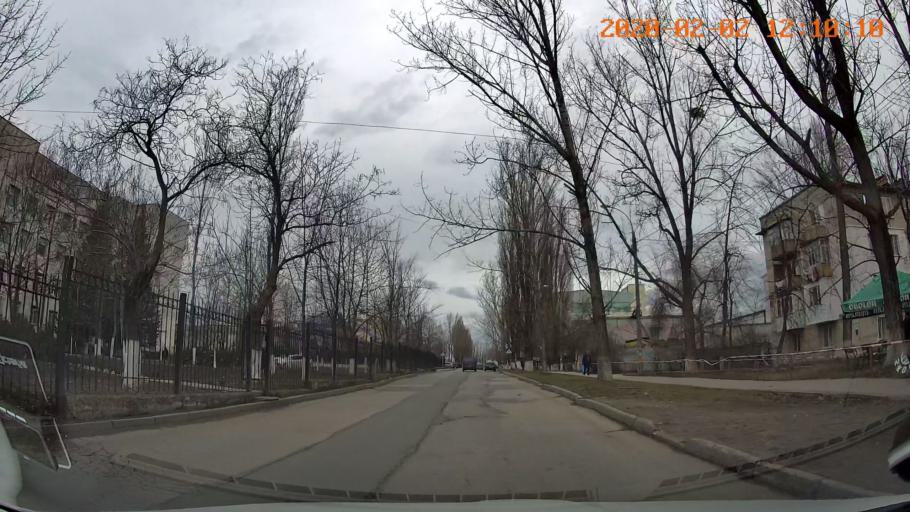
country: MD
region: Chisinau
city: Chisinau
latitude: 46.9990
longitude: 28.8049
